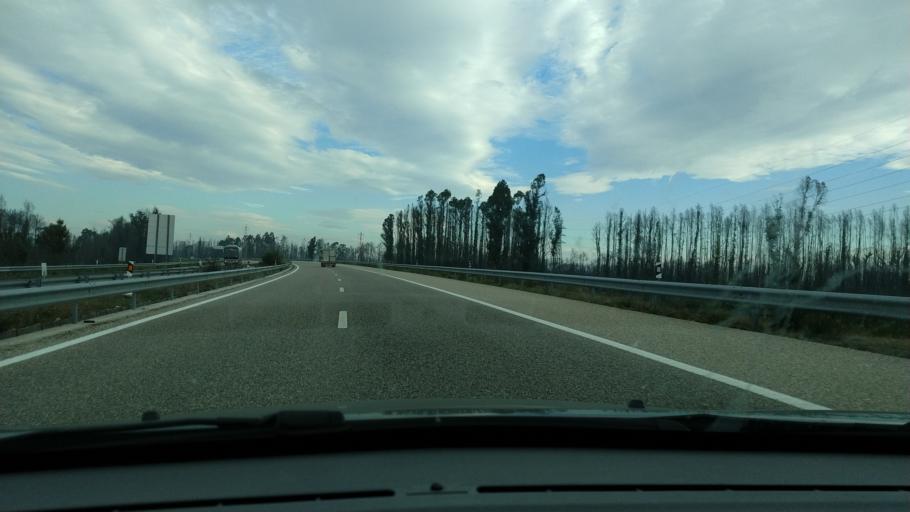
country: PT
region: Coimbra
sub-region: Mira
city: Mira
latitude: 40.4631
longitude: -8.6915
